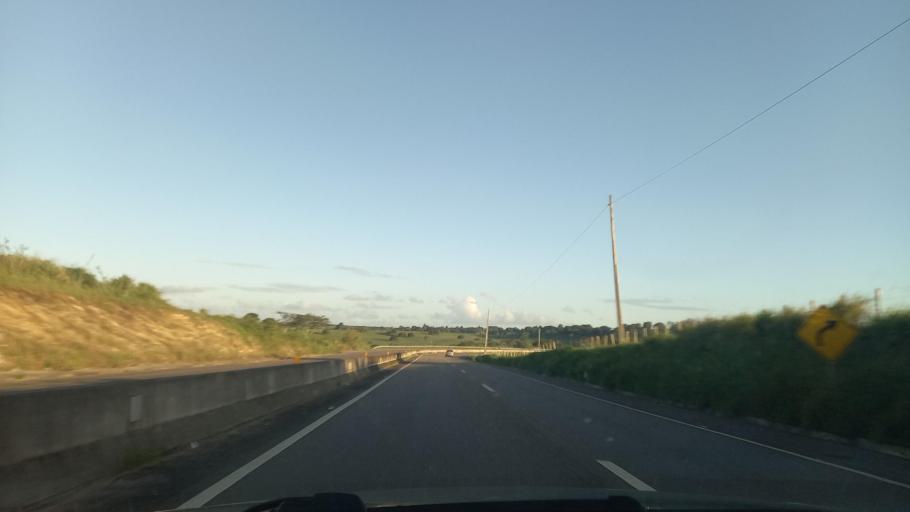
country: BR
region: Alagoas
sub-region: Limoeiro De Anadia
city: Limoeiro de Anadia
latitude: -9.7526
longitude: -36.5032
